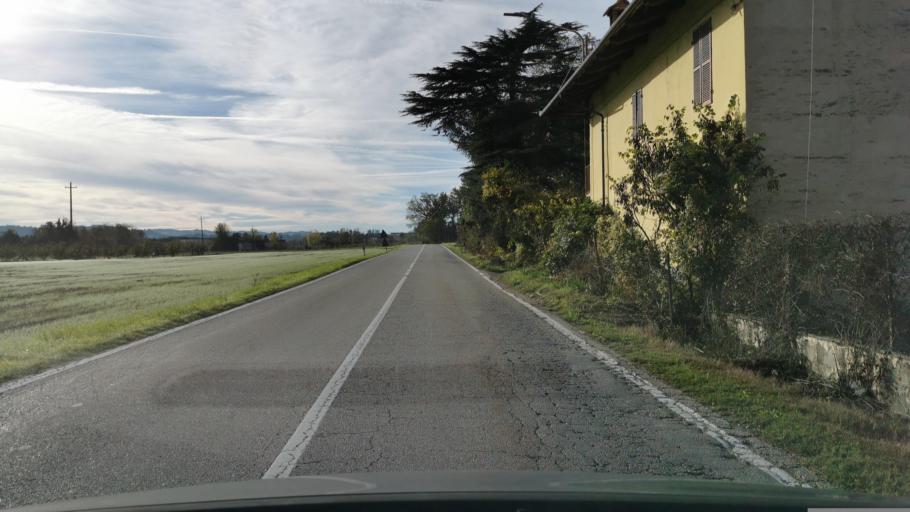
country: IT
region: Piedmont
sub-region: Provincia di Cuneo
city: Narzole
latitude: 44.5921
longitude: 7.8940
